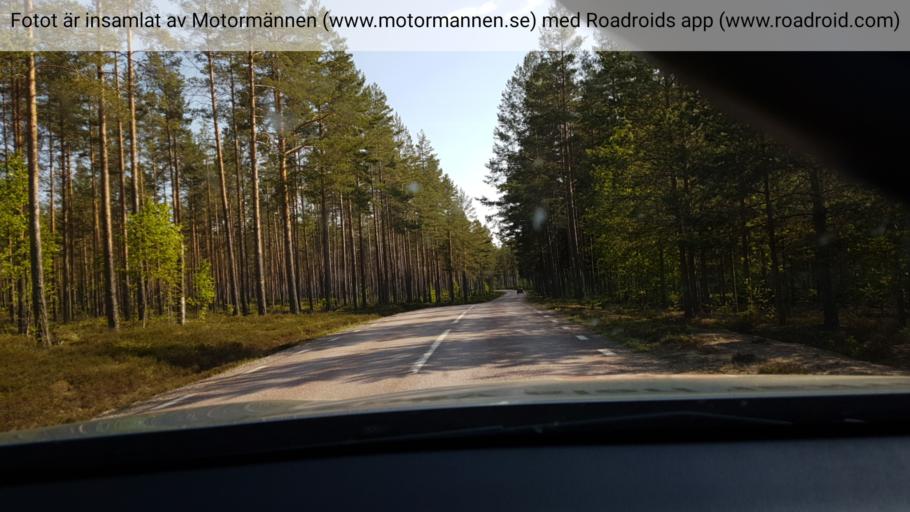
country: SE
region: Gaevleborg
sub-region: Sandvikens Kommun
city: Arsunda
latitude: 60.4895
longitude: 16.7229
